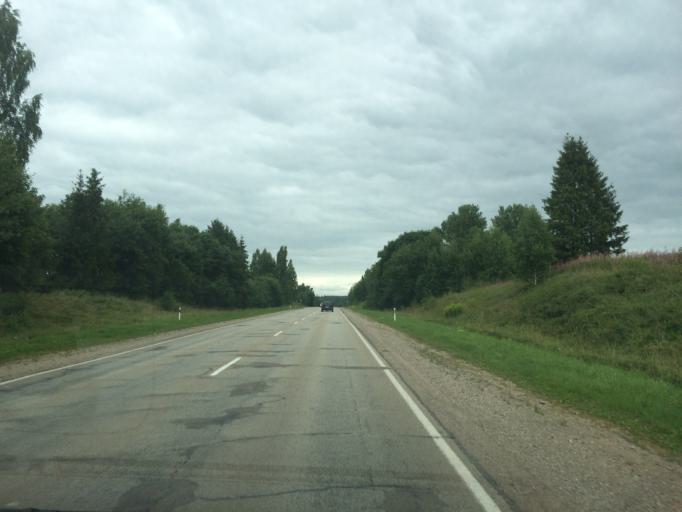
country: LV
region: Rezekne
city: Rezekne
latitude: 56.5576
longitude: 27.3621
